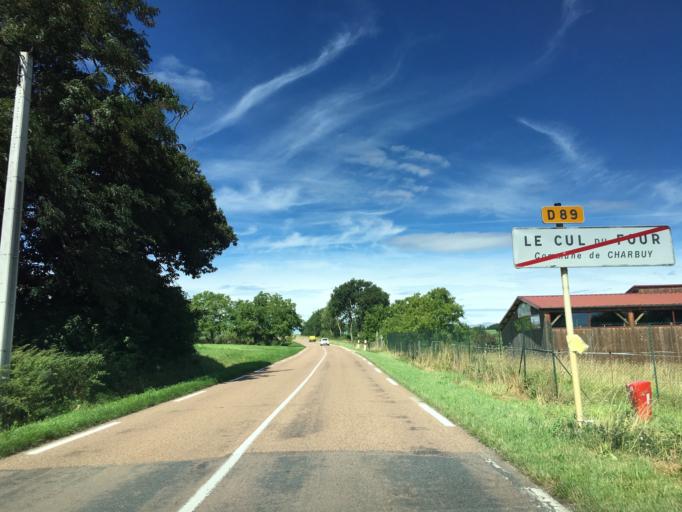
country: FR
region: Bourgogne
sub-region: Departement de l'Yonne
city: Charbuy
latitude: 47.8180
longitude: 3.4581
